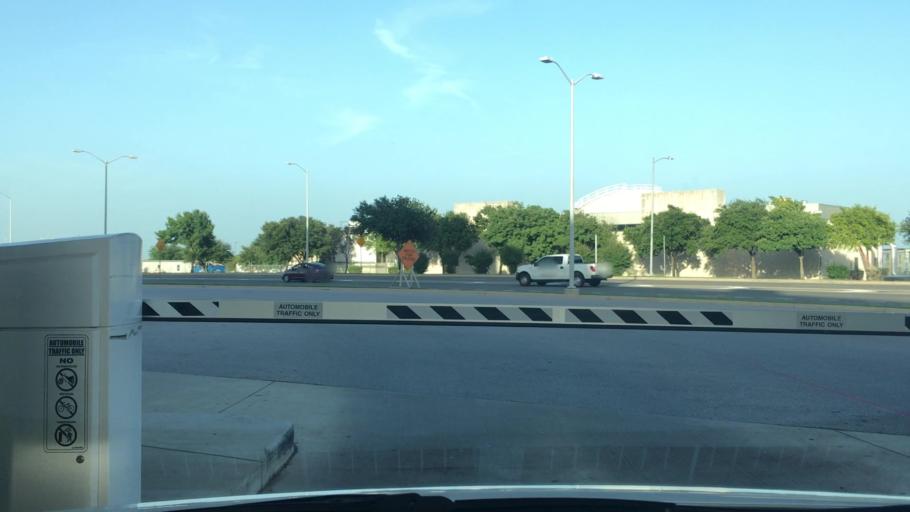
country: US
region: Texas
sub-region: Travis County
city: Hornsby Bend
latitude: 30.2043
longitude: -97.6643
